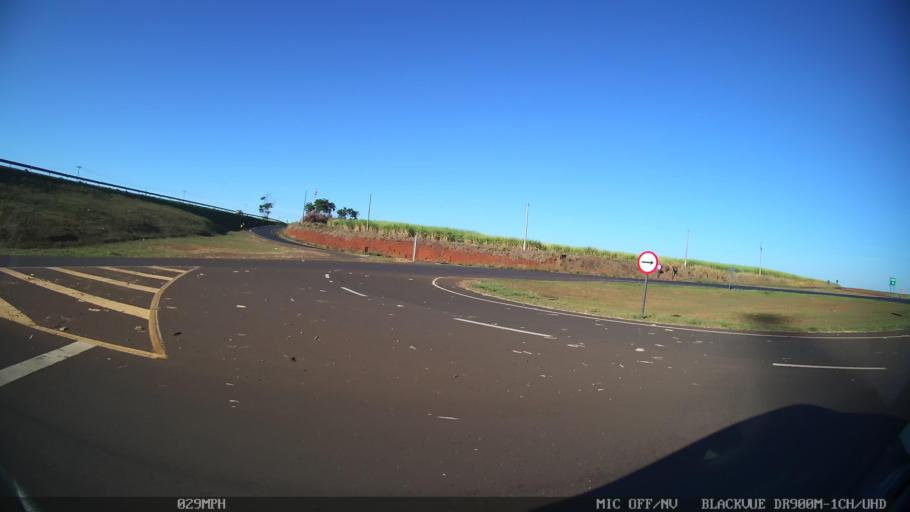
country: BR
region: Sao Paulo
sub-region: Guapiacu
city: Guapiacu
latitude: -20.7377
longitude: -49.0804
